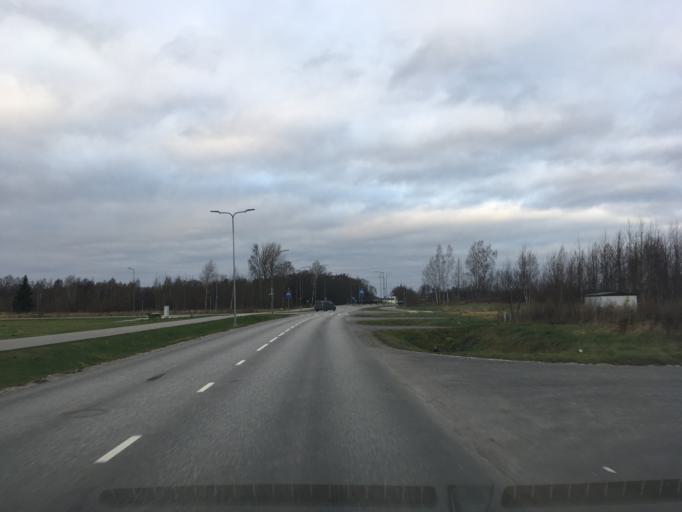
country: EE
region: Paernumaa
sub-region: Paernu linn
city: Parnu
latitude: 58.4011
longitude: 24.4767
